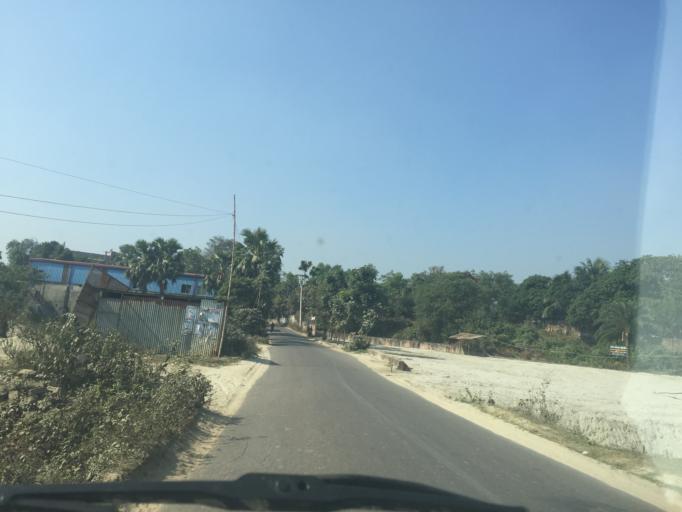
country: BD
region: Dhaka
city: Tungi
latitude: 23.8575
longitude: 90.3265
